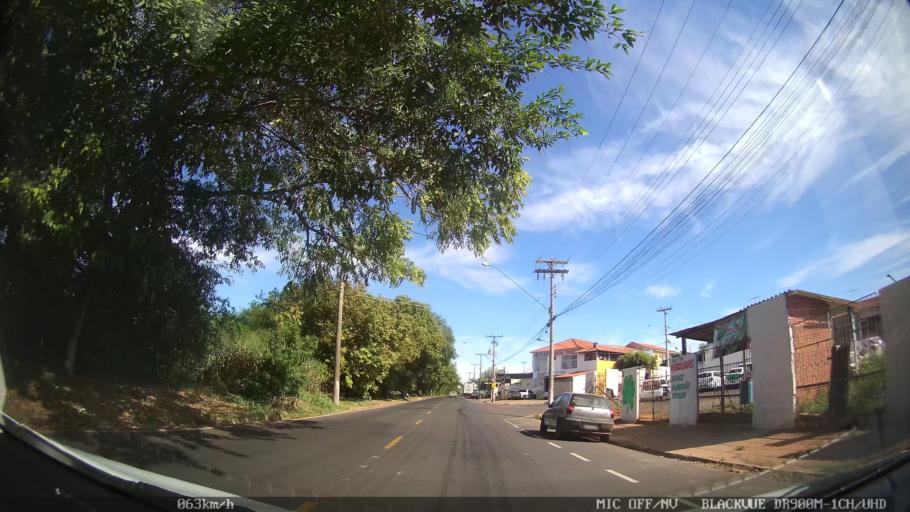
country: BR
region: Sao Paulo
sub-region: Sao Jose Do Rio Preto
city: Sao Jose do Rio Preto
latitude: -20.8468
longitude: -49.3608
